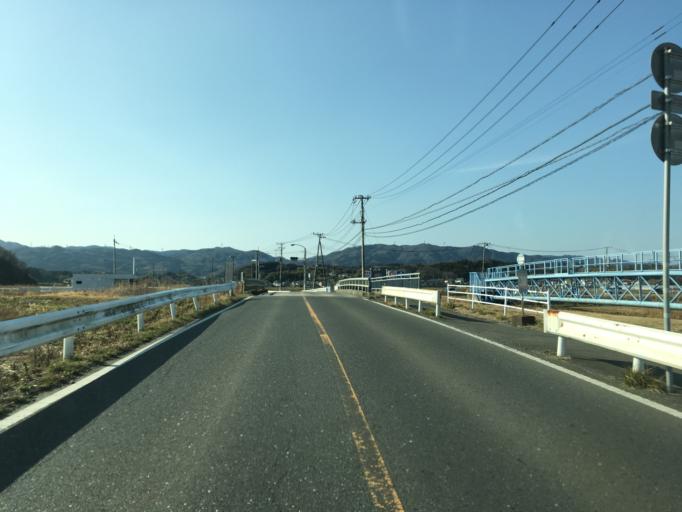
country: JP
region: Ibaraki
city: Kitaibaraki
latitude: 36.7571
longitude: 140.7282
